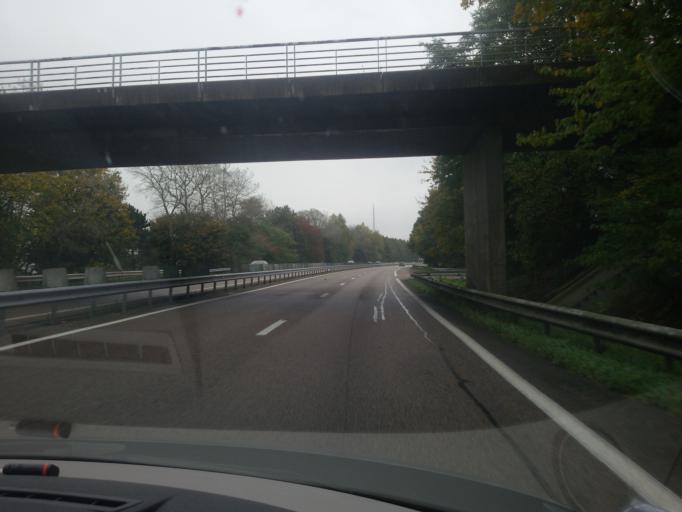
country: FR
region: Haute-Normandie
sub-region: Departement de l'Eure
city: Manneville-sur-Risle
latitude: 49.3948
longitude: 0.5359
